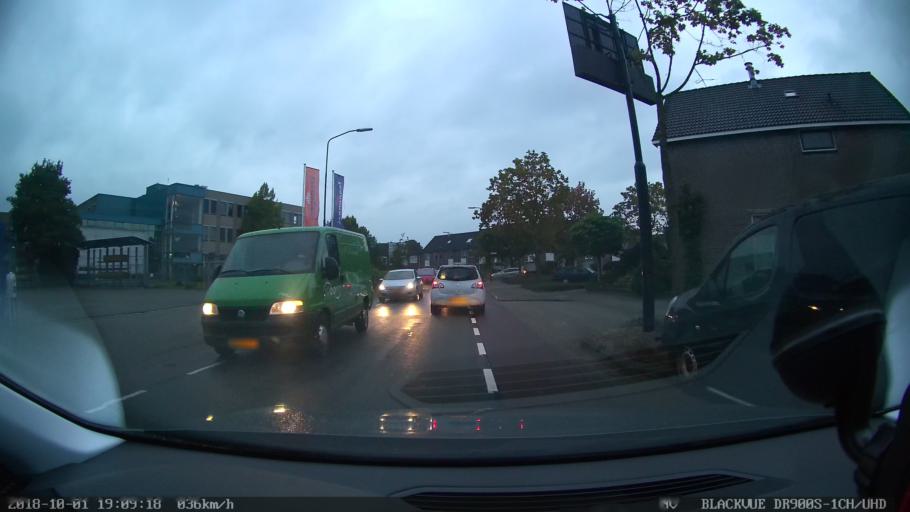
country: NL
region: Gelderland
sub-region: Gemeente Apeldoorn
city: Apeldoorn
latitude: 52.2144
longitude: 5.9829
